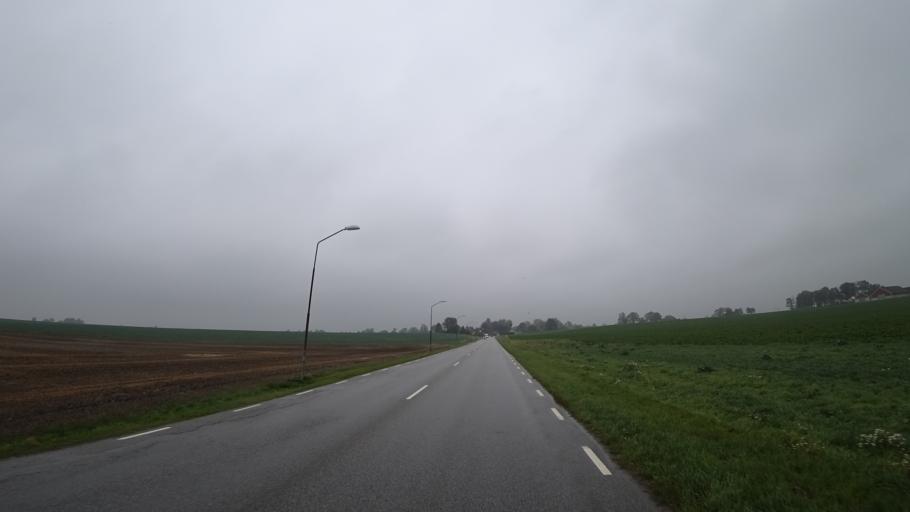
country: SE
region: Skane
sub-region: Kavlinge Kommun
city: Kaevlinge
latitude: 55.7989
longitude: 13.1501
